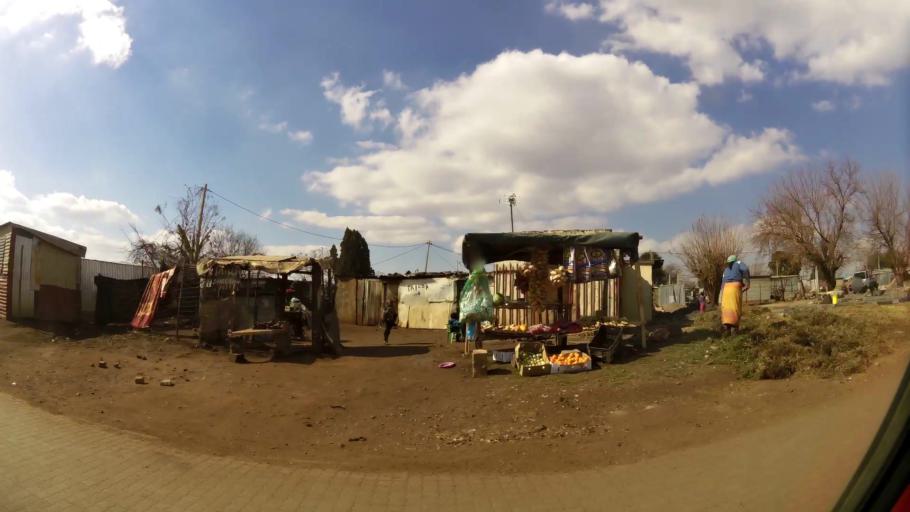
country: ZA
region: Gauteng
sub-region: Ekurhuleni Metropolitan Municipality
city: Tembisa
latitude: -25.9834
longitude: 28.2236
